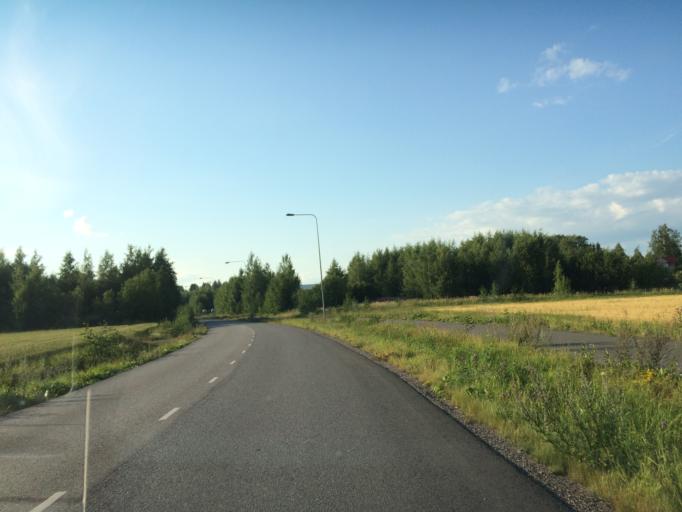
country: FI
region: Haeme
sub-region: Haemeenlinna
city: Parola
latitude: 61.0412
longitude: 24.3813
